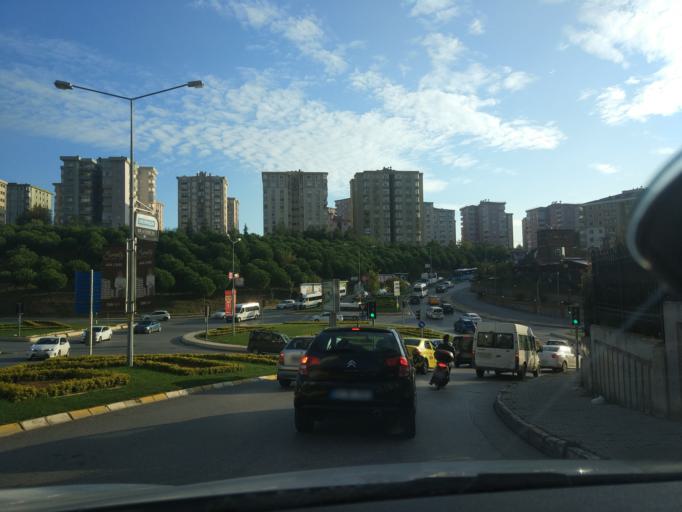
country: TR
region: Istanbul
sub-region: Atasehir
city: Atasehir
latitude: 40.9888
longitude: 29.1253
